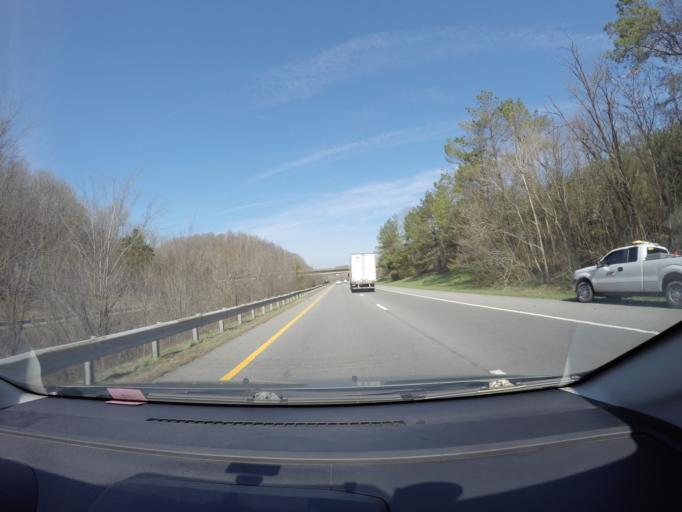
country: US
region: Tennessee
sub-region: Coffee County
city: New Union
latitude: 35.5575
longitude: -86.2023
